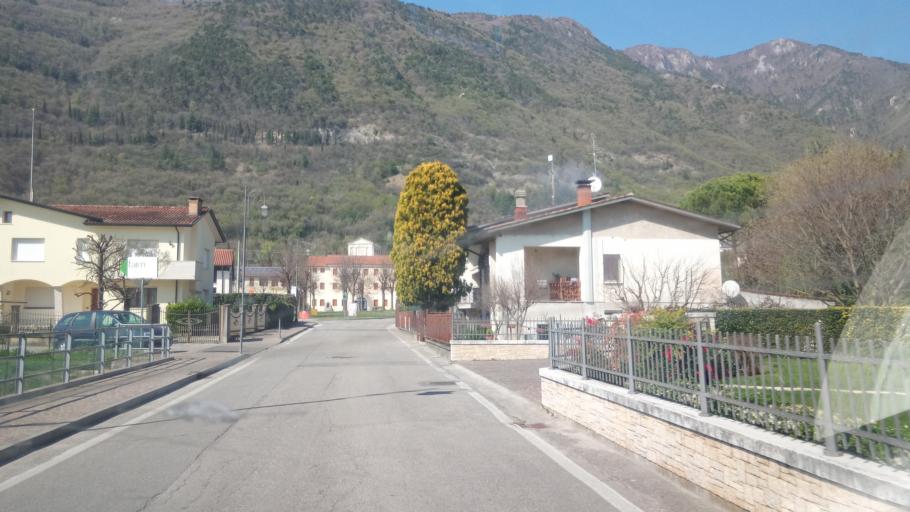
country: IT
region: Veneto
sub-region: Provincia di Treviso
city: Borso del Grappa
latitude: 45.8092
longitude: 11.7730
